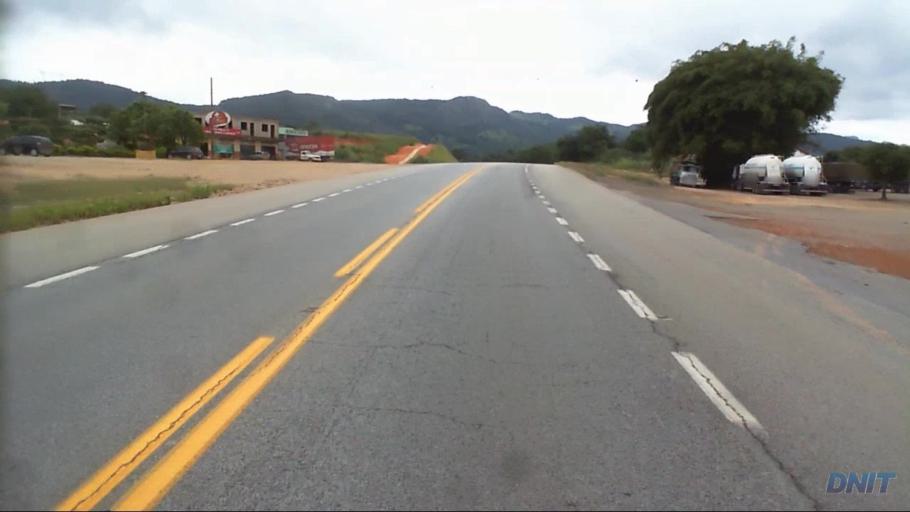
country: BR
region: Minas Gerais
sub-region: Barao De Cocais
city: Barao de Cocais
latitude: -19.7445
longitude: -43.4971
